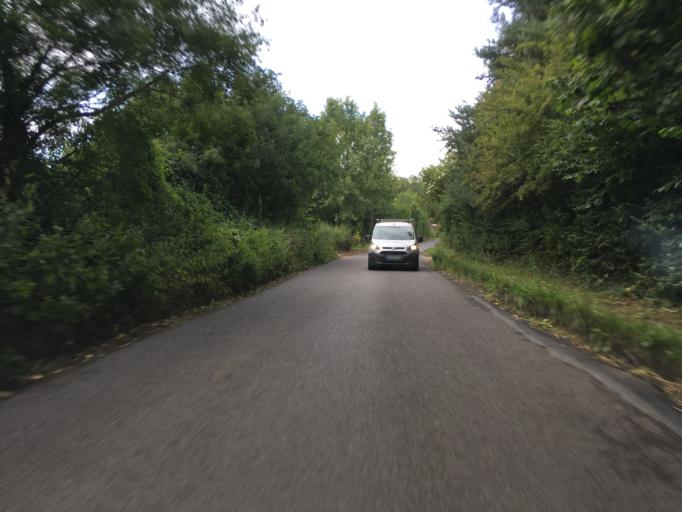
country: GB
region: England
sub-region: Hampshire
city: Colden Common
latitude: 50.9890
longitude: -1.2736
